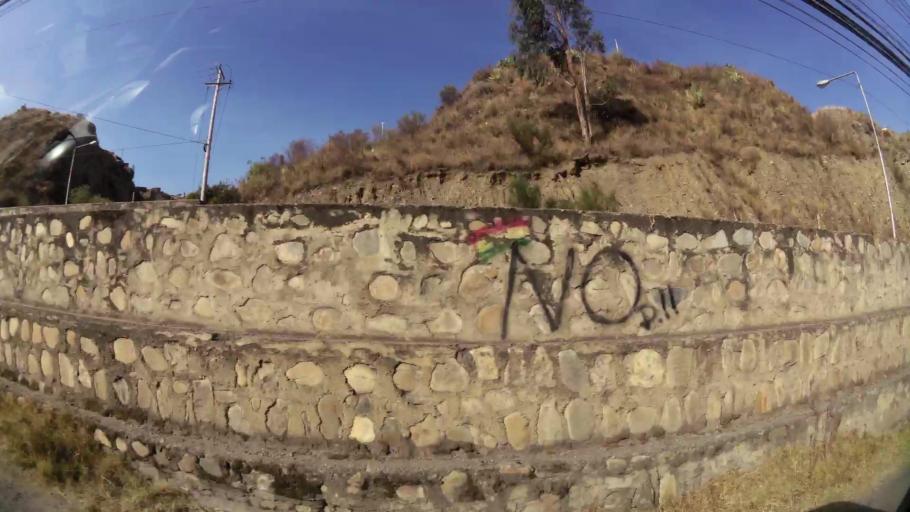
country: BO
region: La Paz
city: La Paz
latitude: -16.5276
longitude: -68.0783
